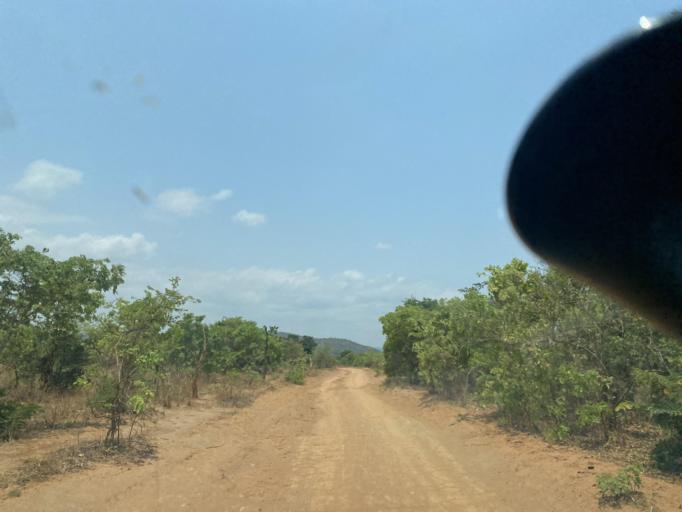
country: ZM
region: Lusaka
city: Chongwe
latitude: -15.5168
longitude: 28.8822
